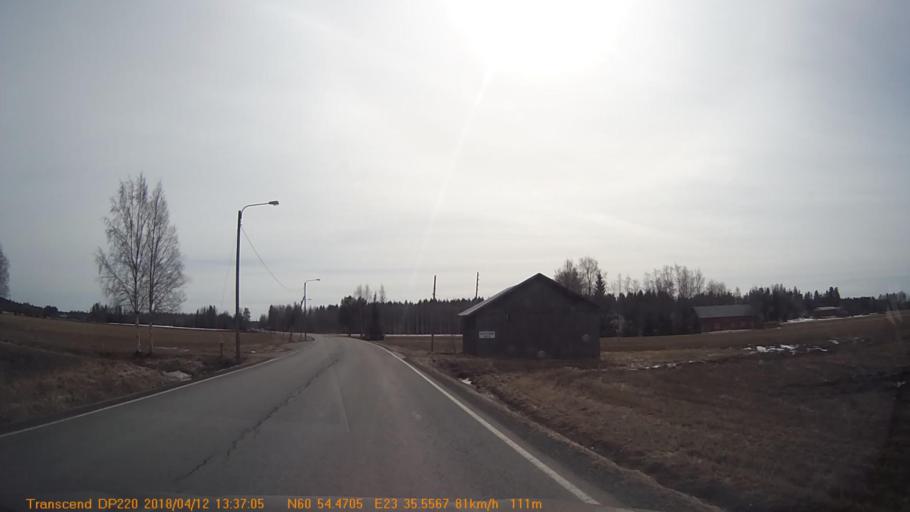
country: FI
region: Haeme
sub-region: Forssa
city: Forssa
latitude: 60.9075
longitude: 23.5926
